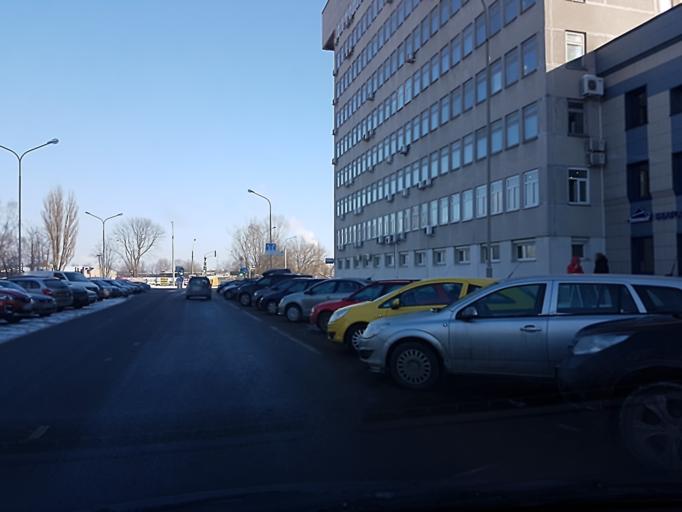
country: BY
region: Minsk
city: Minsk
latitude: 53.9113
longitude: 27.5164
